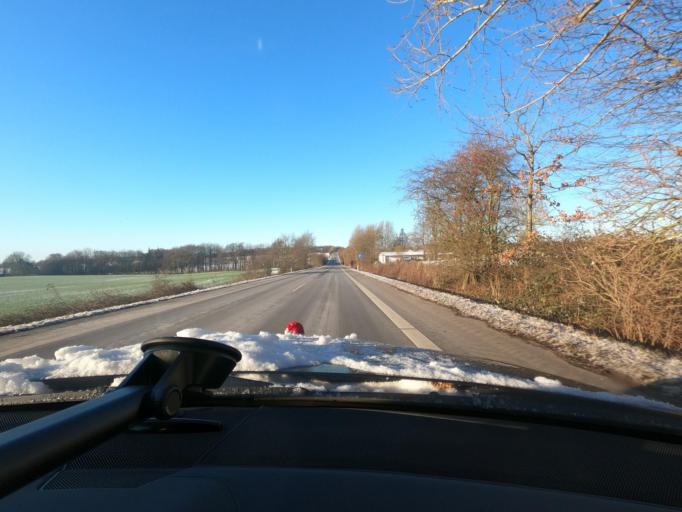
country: DK
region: South Denmark
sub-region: Sonderborg Kommune
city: Horuphav
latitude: 54.9074
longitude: 9.9298
